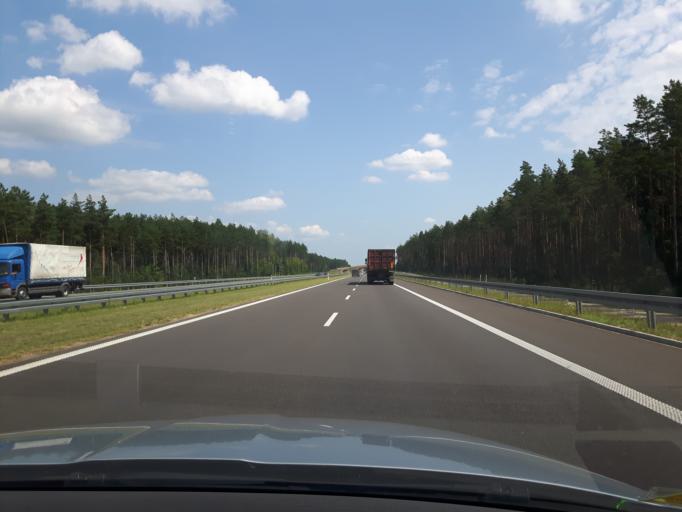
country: PL
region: Warmian-Masurian Voivodeship
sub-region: Powiat olsztynski
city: Olsztynek
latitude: 53.5848
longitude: 20.1943
